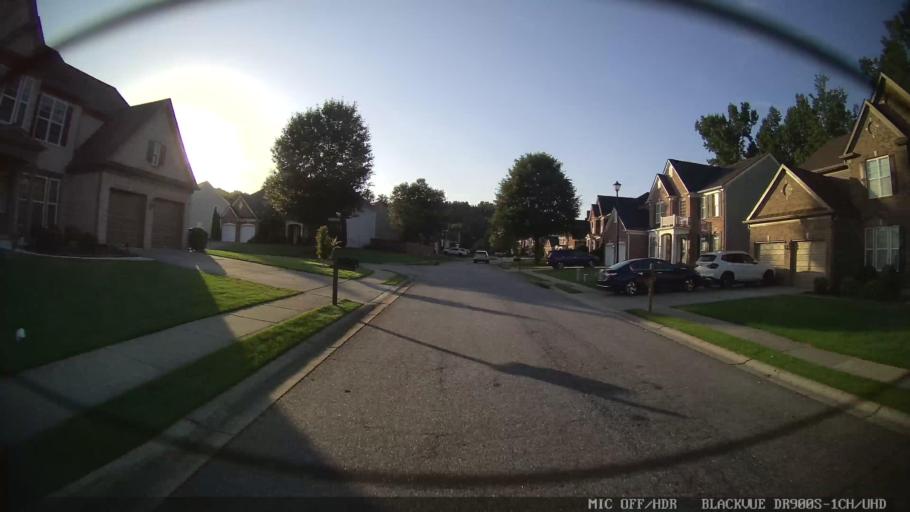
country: US
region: Georgia
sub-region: Forsyth County
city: Cumming
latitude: 34.2163
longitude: -84.2320
